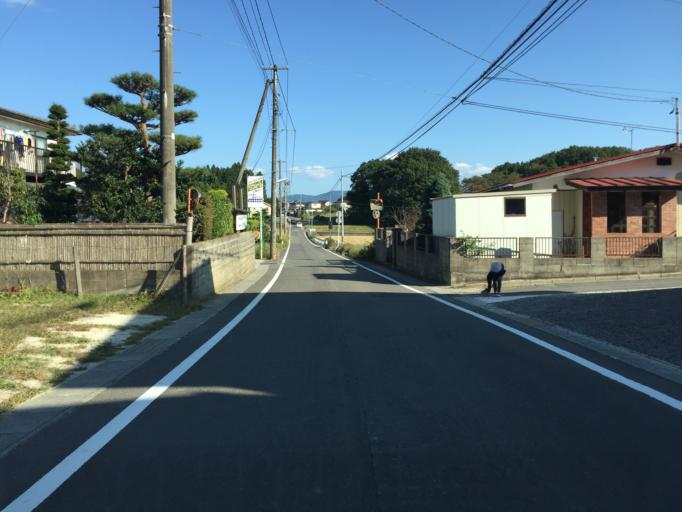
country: JP
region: Fukushima
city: Nihommatsu
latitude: 37.6555
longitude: 140.4678
